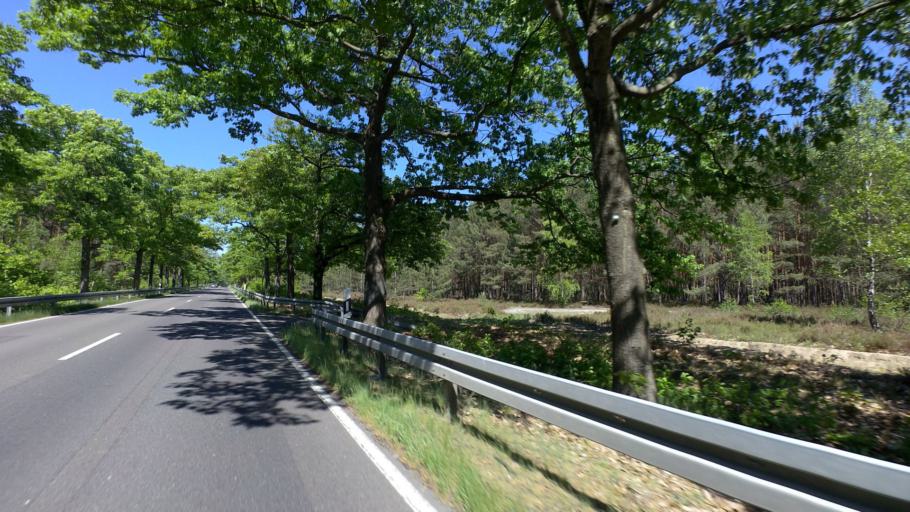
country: DE
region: Brandenburg
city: Drachhausen
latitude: 51.9163
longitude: 14.3502
